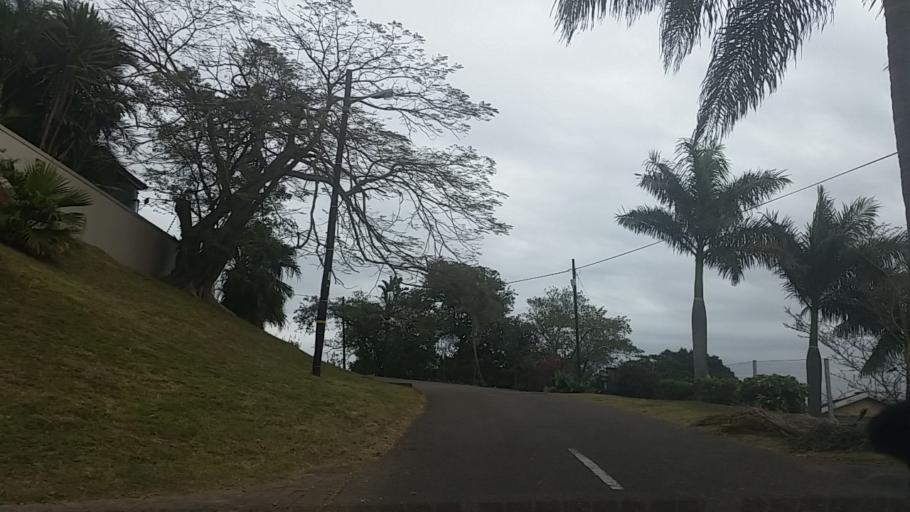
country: ZA
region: KwaZulu-Natal
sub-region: eThekwini Metropolitan Municipality
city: Berea
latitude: -29.8420
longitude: 30.9313
